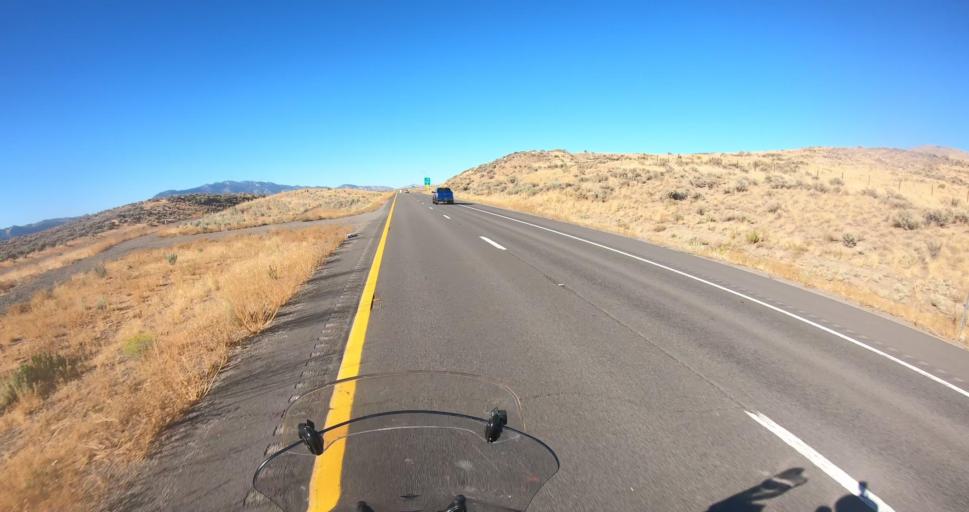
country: US
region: Nevada
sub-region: Washoe County
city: Cold Springs
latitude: 39.7694
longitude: -120.0383
